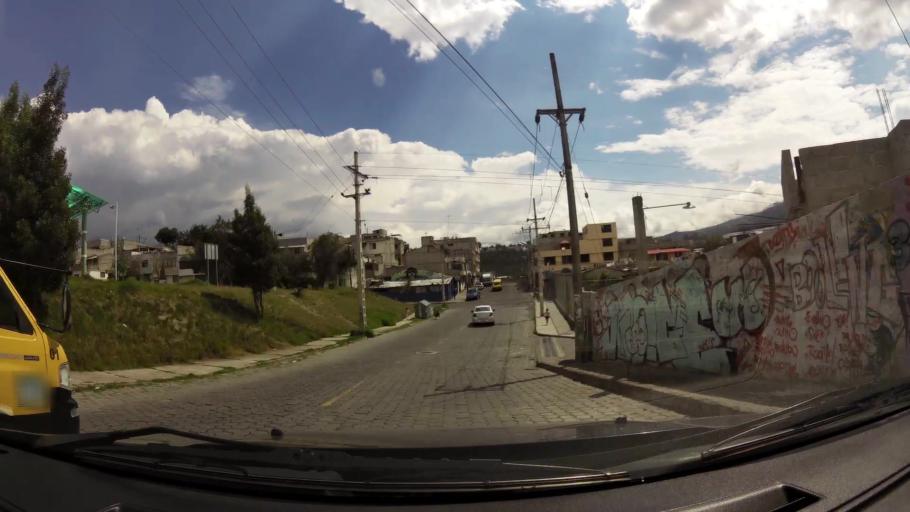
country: EC
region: Pichincha
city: Quito
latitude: -0.0894
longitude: -78.4510
